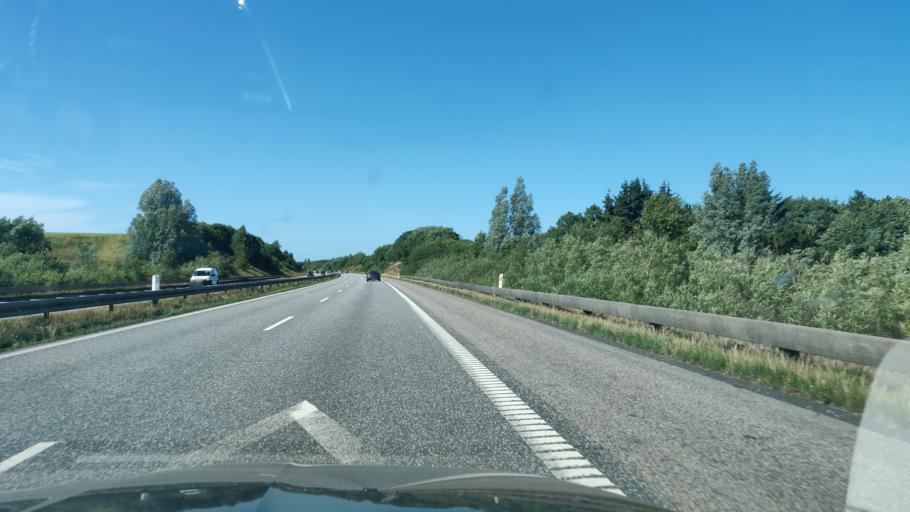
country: DK
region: North Denmark
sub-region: Mariagerfjord Kommune
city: Hobro
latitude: 56.7035
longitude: 9.7296
